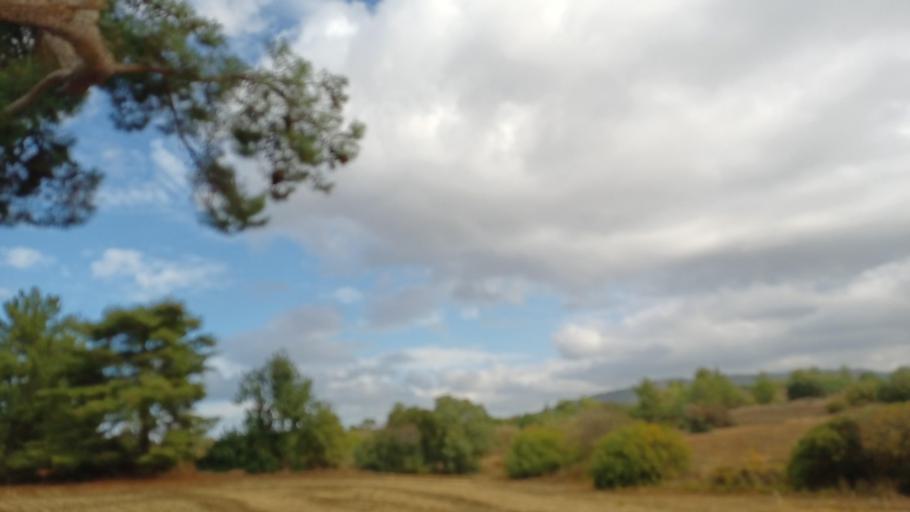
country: CY
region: Pafos
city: Polis
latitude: 35.0080
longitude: 32.4954
